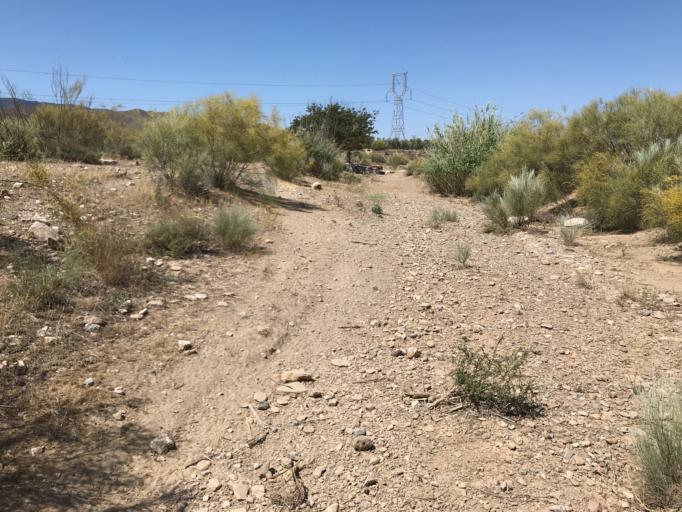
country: ES
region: Andalusia
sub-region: Provincia de Almeria
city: Turrillas
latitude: 37.0741
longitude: -2.2999
